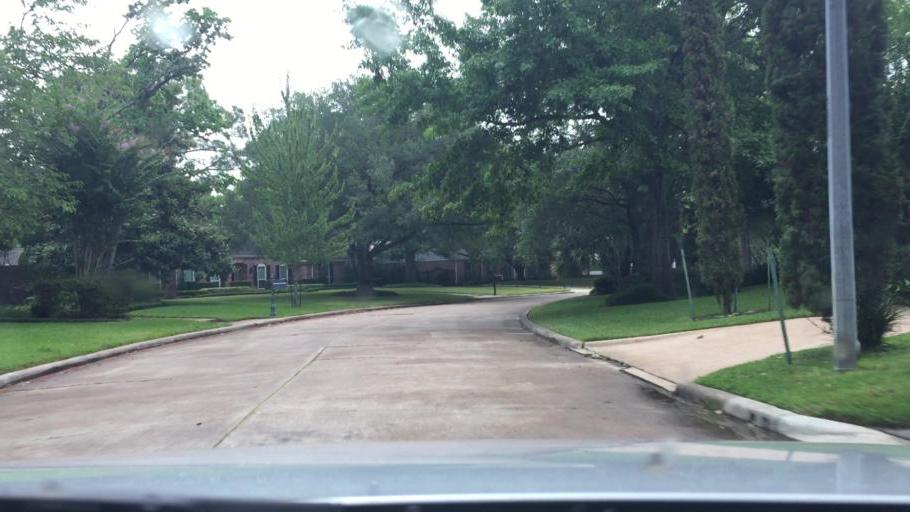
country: US
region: Texas
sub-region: Harris County
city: Hunters Creek Village
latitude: 29.7672
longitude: -95.5065
